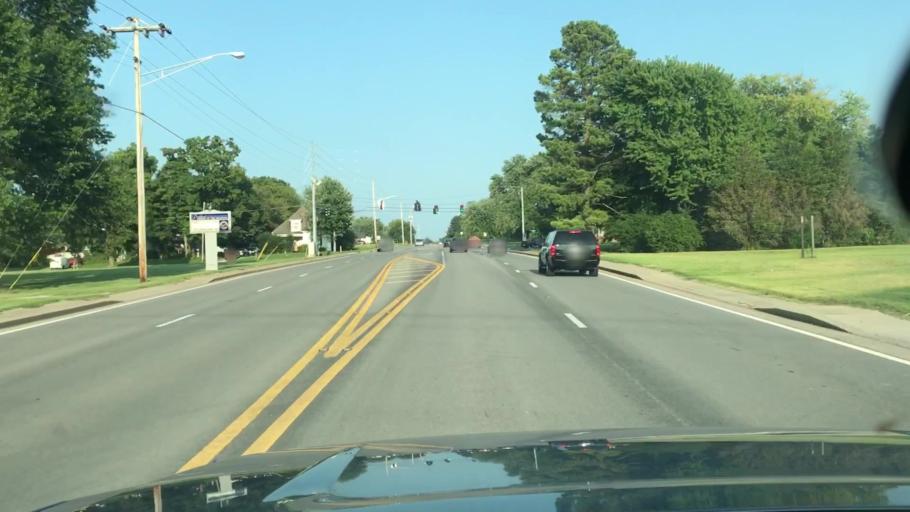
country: US
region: Tennessee
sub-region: Sumner County
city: Portland
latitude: 36.5776
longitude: -86.5088
